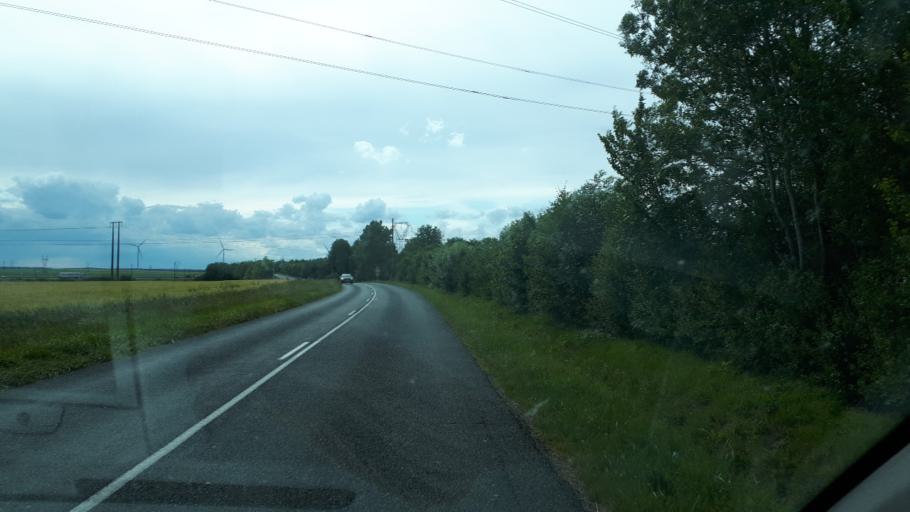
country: FR
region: Centre
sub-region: Departement du Cher
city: Marmagne
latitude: 47.0805
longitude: 2.2772
